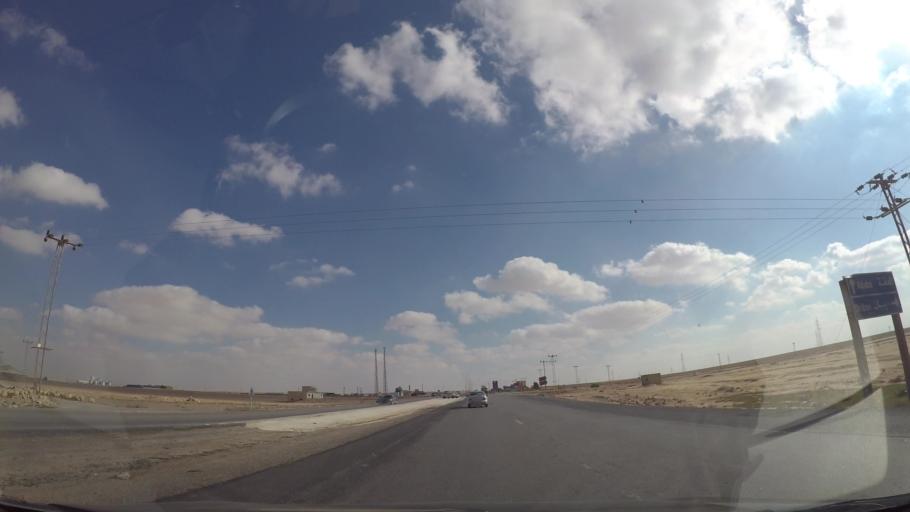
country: JO
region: Amman
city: Al Jizah
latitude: 31.4969
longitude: 36.0582
